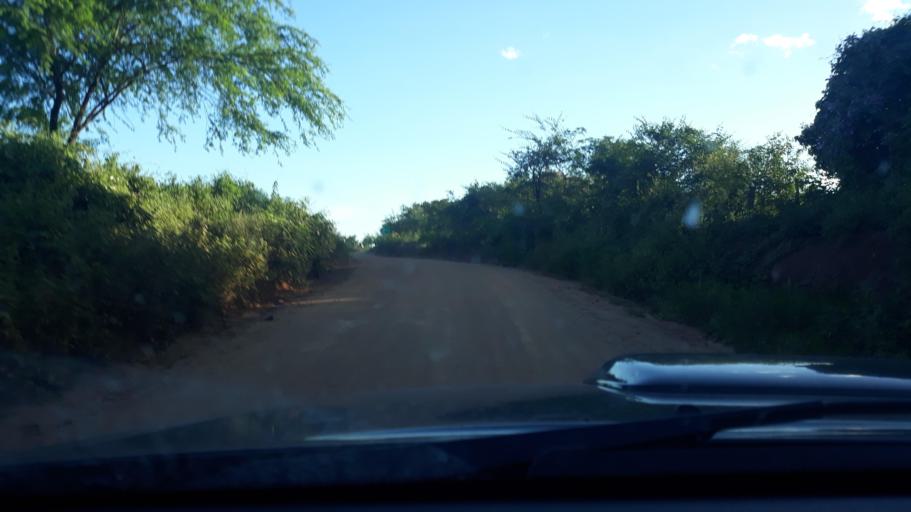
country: BR
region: Bahia
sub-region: Riacho De Santana
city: Riacho de Santana
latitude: -13.7996
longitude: -42.7128
